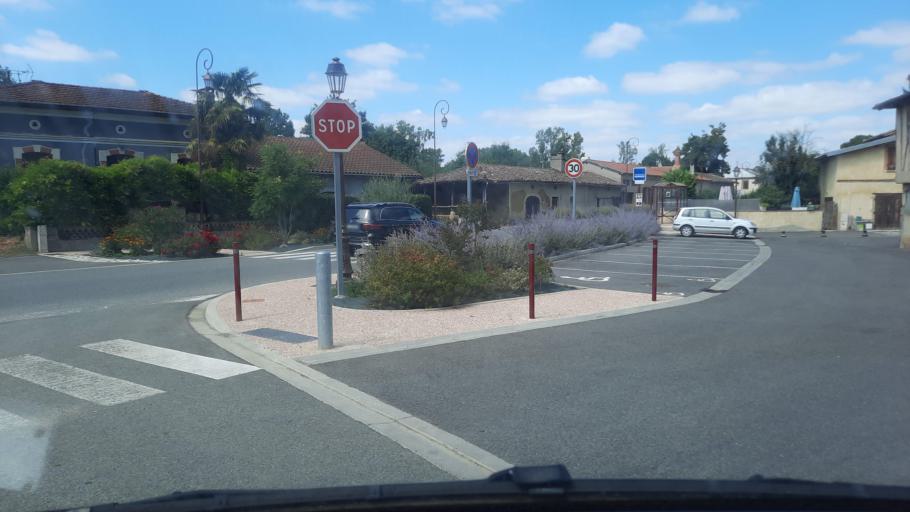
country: FR
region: Midi-Pyrenees
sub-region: Departement du Gers
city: Samatan
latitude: 43.5191
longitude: 0.9808
